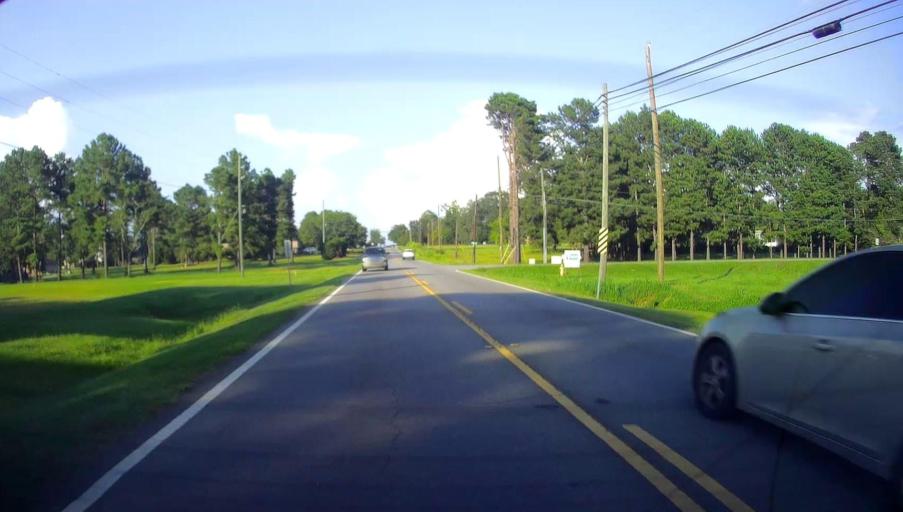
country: US
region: Georgia
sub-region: Houston County
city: Perry
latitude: 32.4707
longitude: -83.7125
